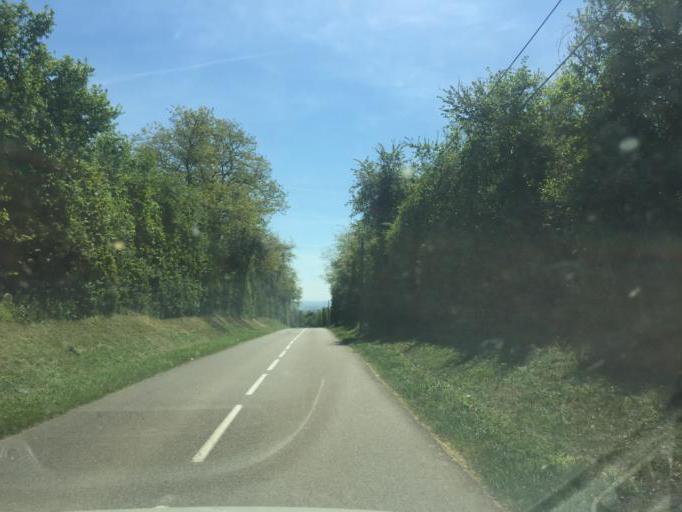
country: FR
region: Rhone-Alpes
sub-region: Departement de l'Ain
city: Beynost
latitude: 45.8468
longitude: 4.9940
